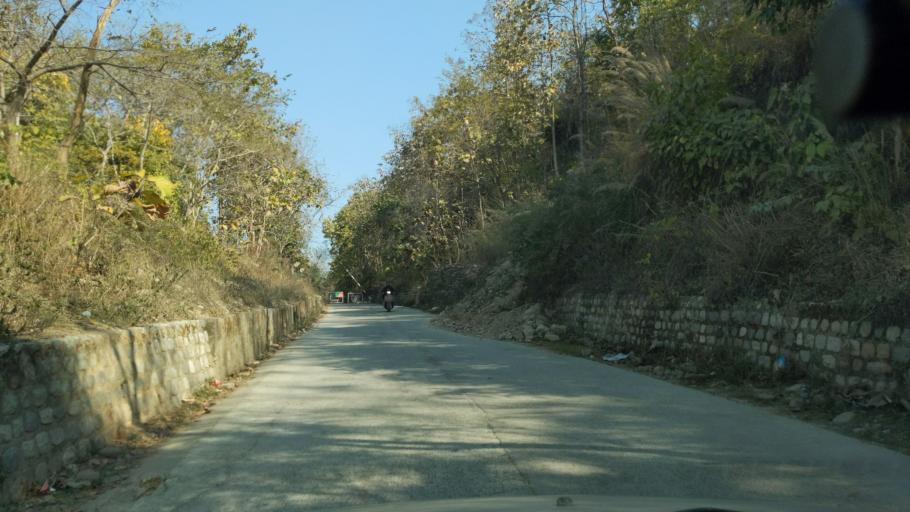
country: IN
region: Uttarakhand
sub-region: Naini Tal
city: Ramnagar
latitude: 29.3989
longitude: 79.1351
